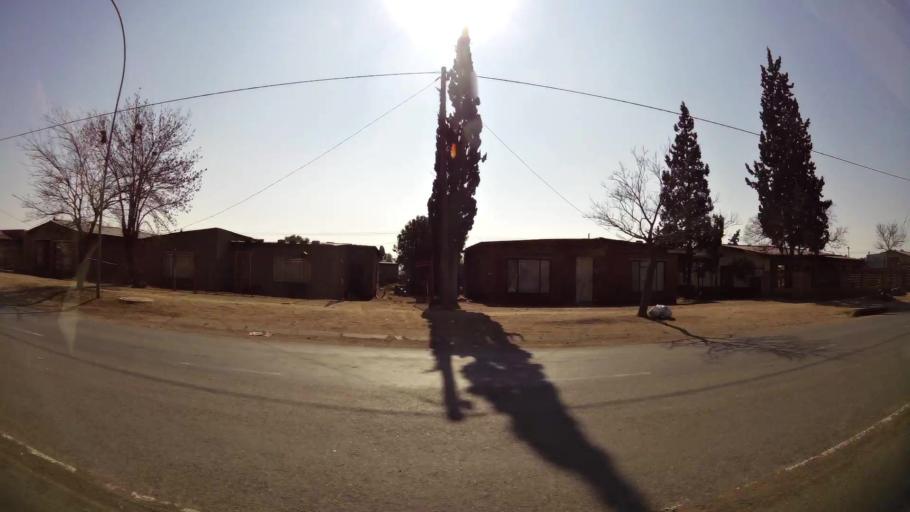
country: ZA
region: Orange Free State
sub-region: Mangaung Metropolitan Municipality
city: Bloemfontein
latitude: -29.1564
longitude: 26.2429
